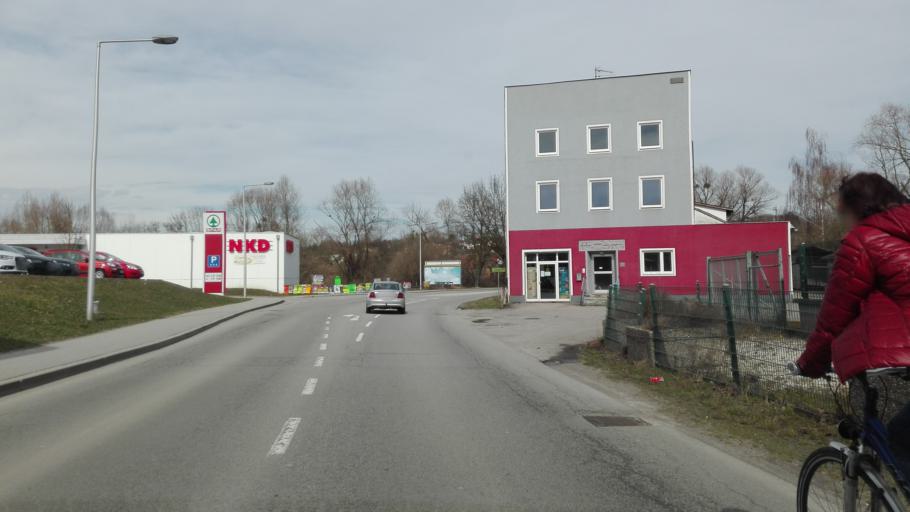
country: AT
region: Upper Austria
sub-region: Politischer Bezirk Scharding
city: Scharding
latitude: 48.4643
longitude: 13.4360
